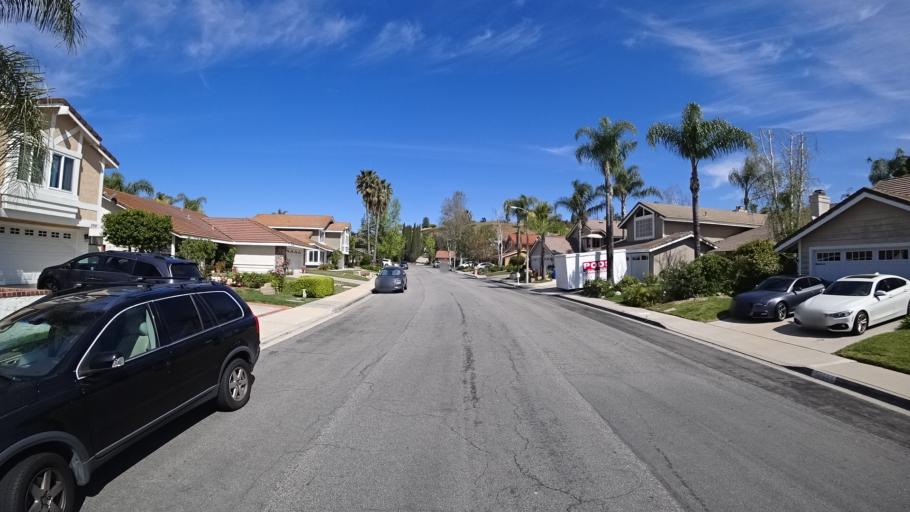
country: US
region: California
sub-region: Ventura County
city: Thousand Oaks
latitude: 34.2189
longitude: -118.8381
